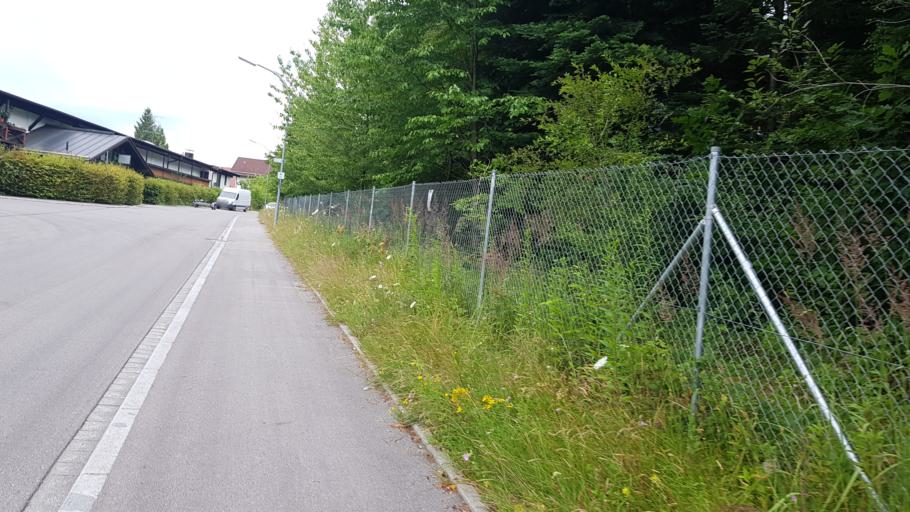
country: DE
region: Bavaria
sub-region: Upper Bavaria
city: Grafrath
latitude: 48.1342
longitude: 11.1629
